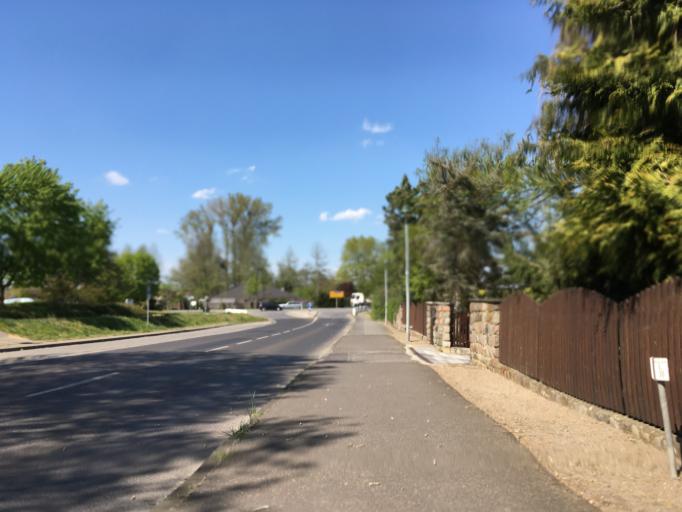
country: DE
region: Brandenburg
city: Werneuchen
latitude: 52.6210
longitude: 13.6746
